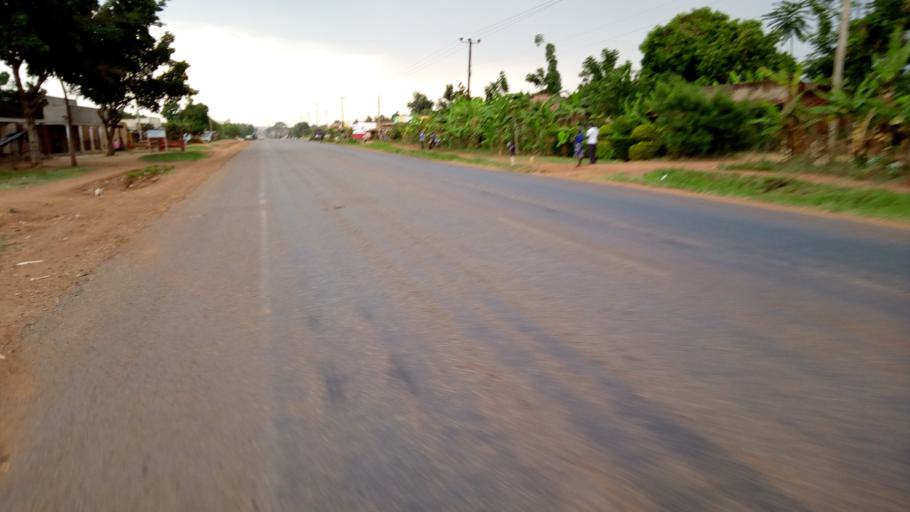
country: UG
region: Eastern Region
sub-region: Mbale District
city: Mbale
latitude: 1.1173
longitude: 34.1704
